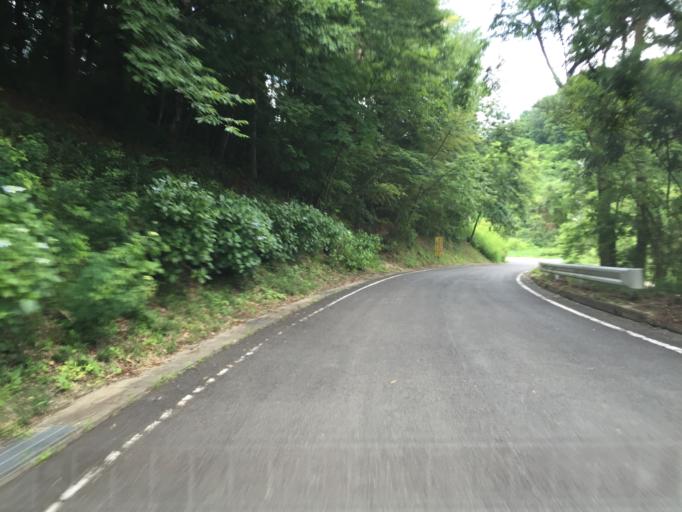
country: JP
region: Fukushima
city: Fukushima-shi
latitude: 37.6800
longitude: 140.5123
